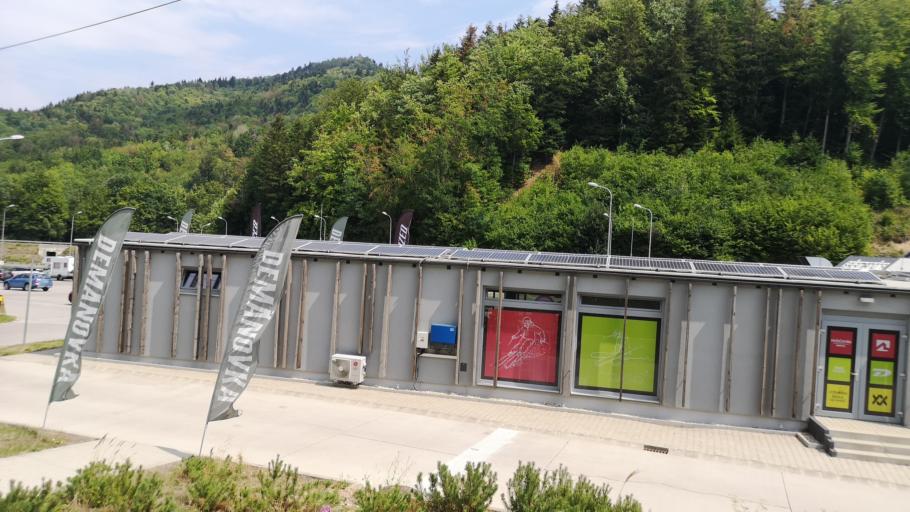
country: SK
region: Banskobystricky
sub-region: Okres Banska Bystrica
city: Banska Stiavnica
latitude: 48.4577
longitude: 18.8530
